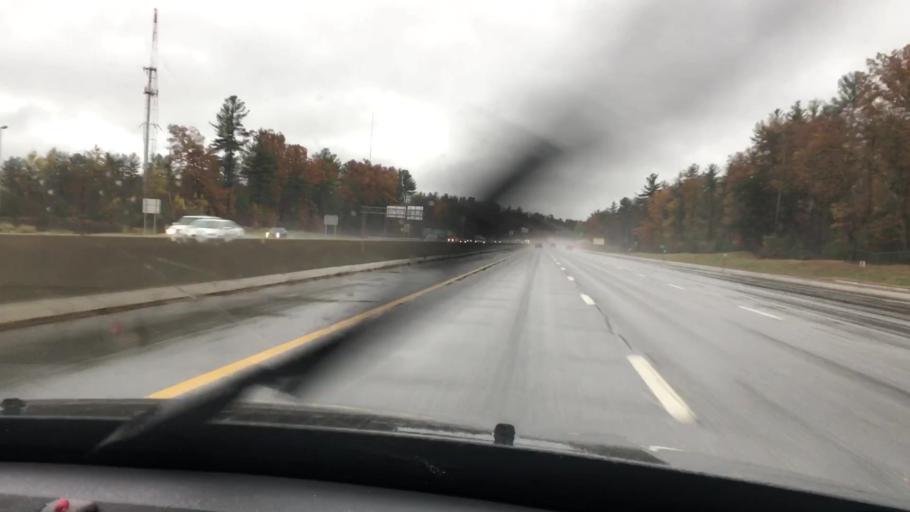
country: US
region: New Hampshire
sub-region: Hillsborough County
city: East Merrimack
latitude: 42.9111
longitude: -71.4646
